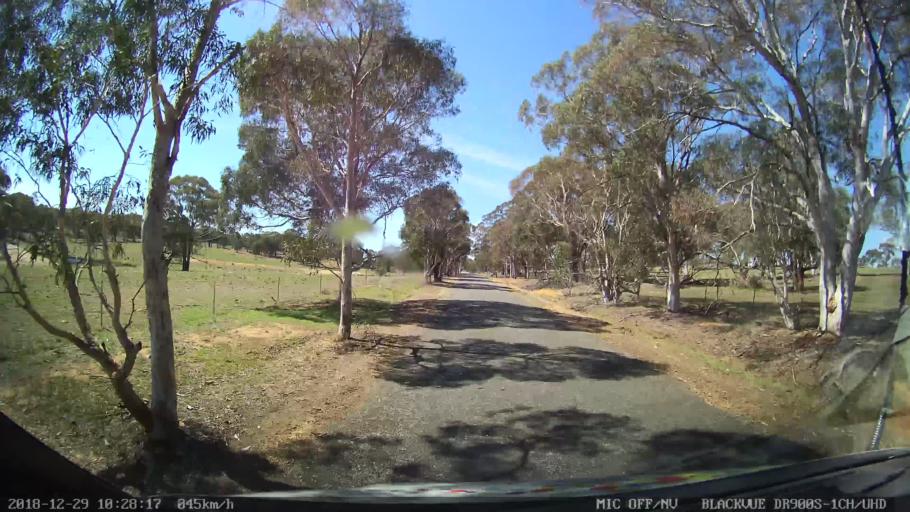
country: AU
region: New South Wales
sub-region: Yass Valley
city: Gundaroo
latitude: -34.9412
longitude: 149.4541
